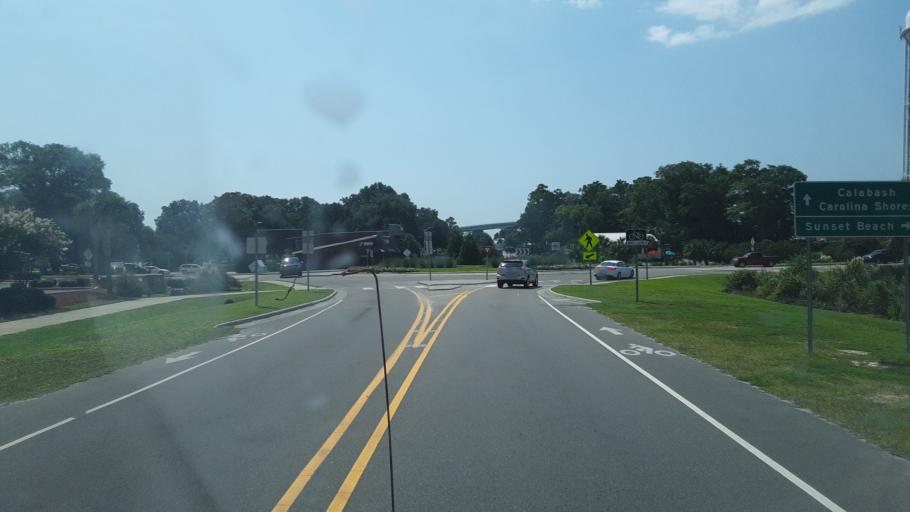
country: US
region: North Carolina
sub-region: Brunswick County
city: Sunset Beach
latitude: 33.8862
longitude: -78.5108
